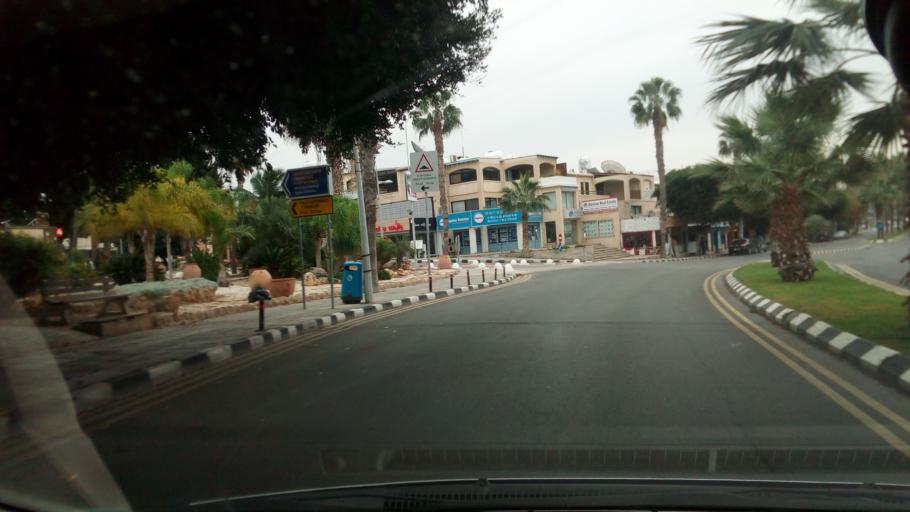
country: CY
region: Pafos
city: Paphos
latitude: 34.7553
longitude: 32.4190
